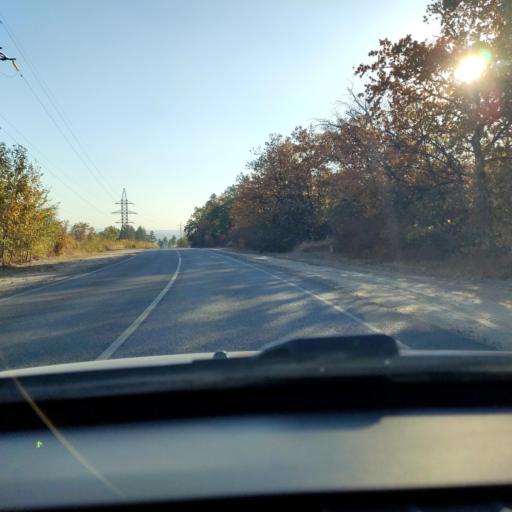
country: RU
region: Voronezj
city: Shilovo
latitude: 51.5601
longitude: 39.1380
